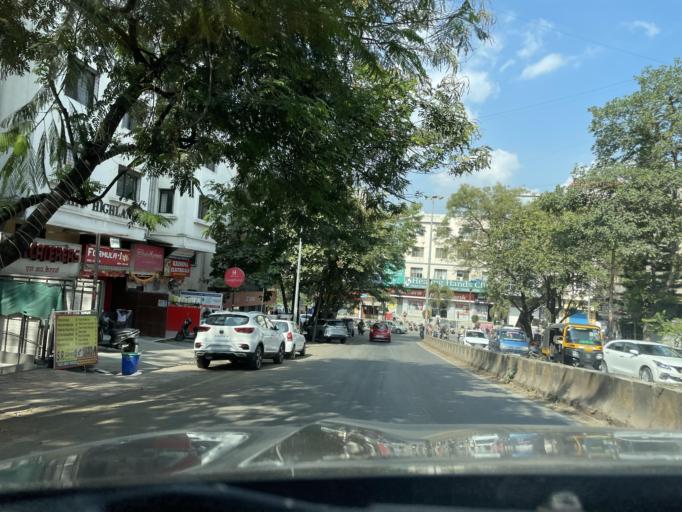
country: IN
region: Maharashtra
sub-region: Pune Division
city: Pune
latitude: 18.4808
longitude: 73.9015
